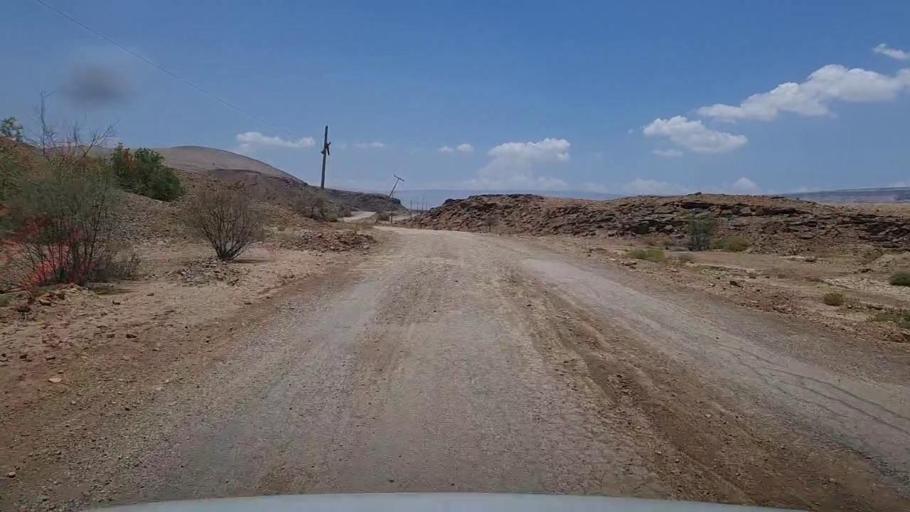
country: PK
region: Sindh
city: Bhan
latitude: 26.3183
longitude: 67.5435
